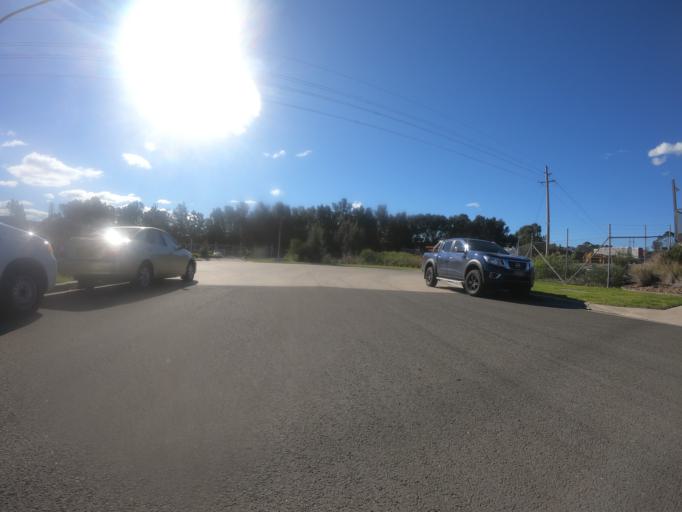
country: AU
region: New South Wales
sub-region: Wollongong
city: Berkeley
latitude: -34.4627
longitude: 150.8575
